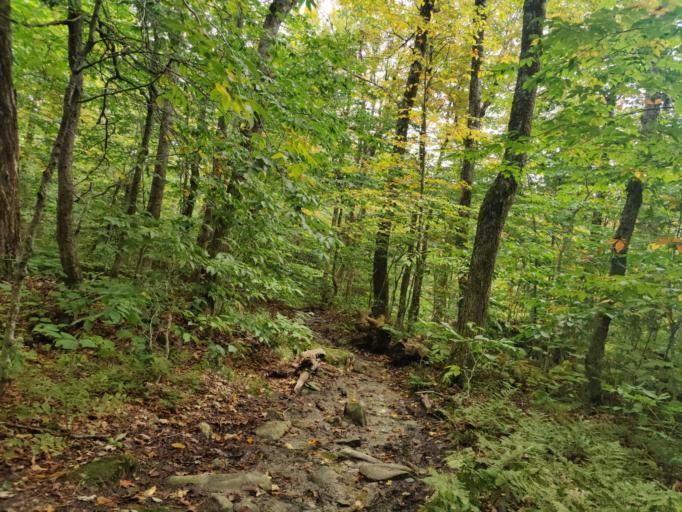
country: US
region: Vermont
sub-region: Bennington County
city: Manchester Center
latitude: 43.2648
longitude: -72.9408
